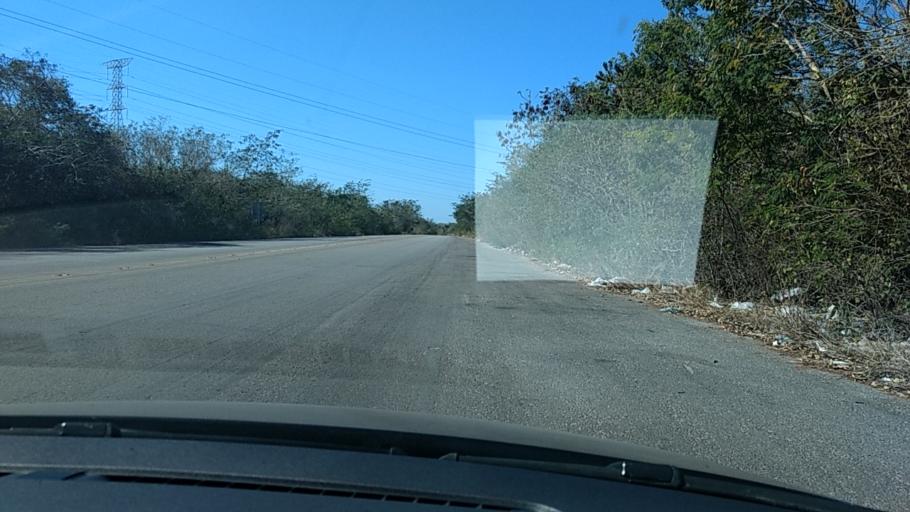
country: MX
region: Yucatan
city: Valladolid
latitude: 20.7024
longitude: -88.2413
